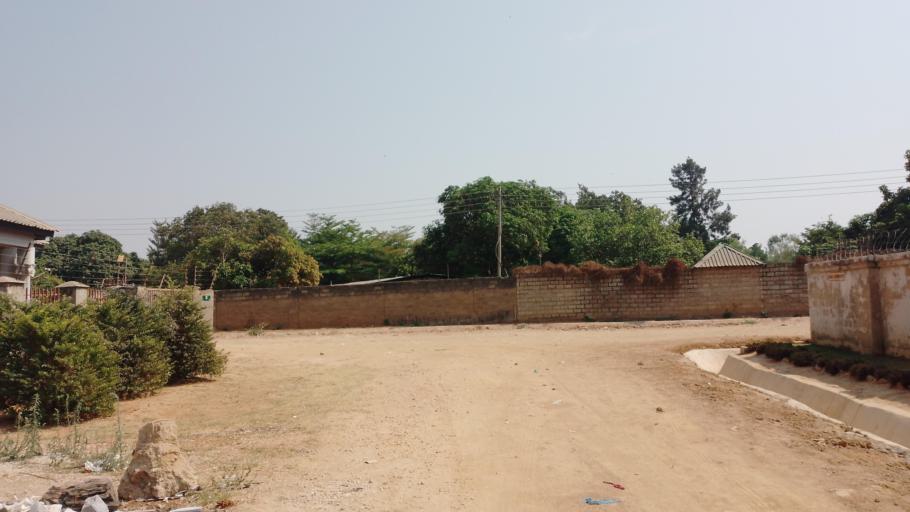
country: ZM
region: Lusaka
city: Lusaka
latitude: -15.3872
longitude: 28.3904
